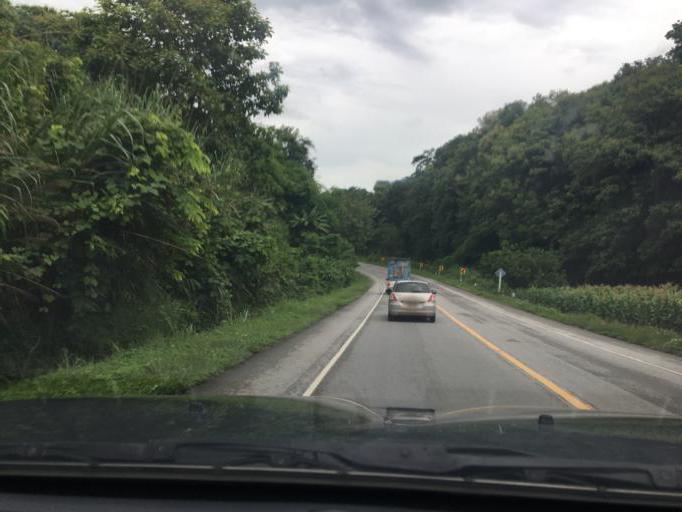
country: TH
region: Chiang Rai
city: Wiang Pa Pao
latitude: 19.4437
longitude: 99.4997
